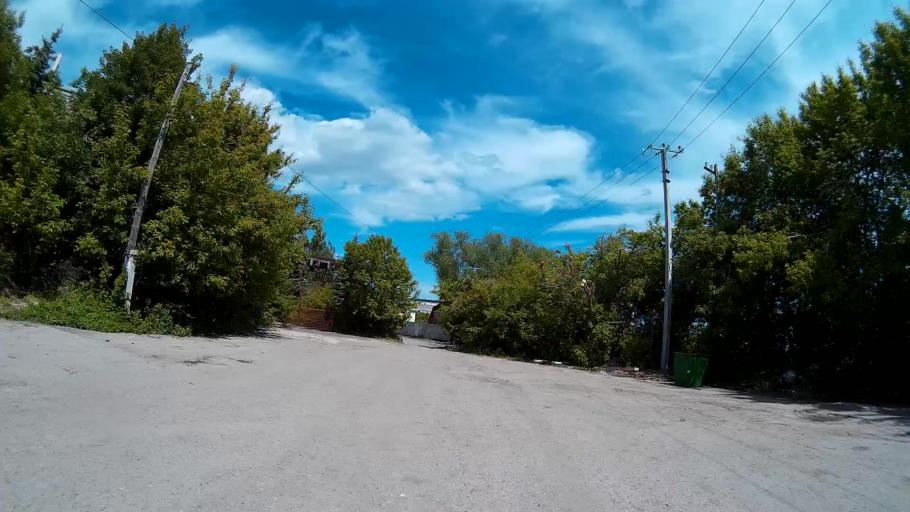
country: RU
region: Ulyanovsk
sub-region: Ulyanovskiy Rayon
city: Ulyanovsk
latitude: 54.2778
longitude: 48.3526
